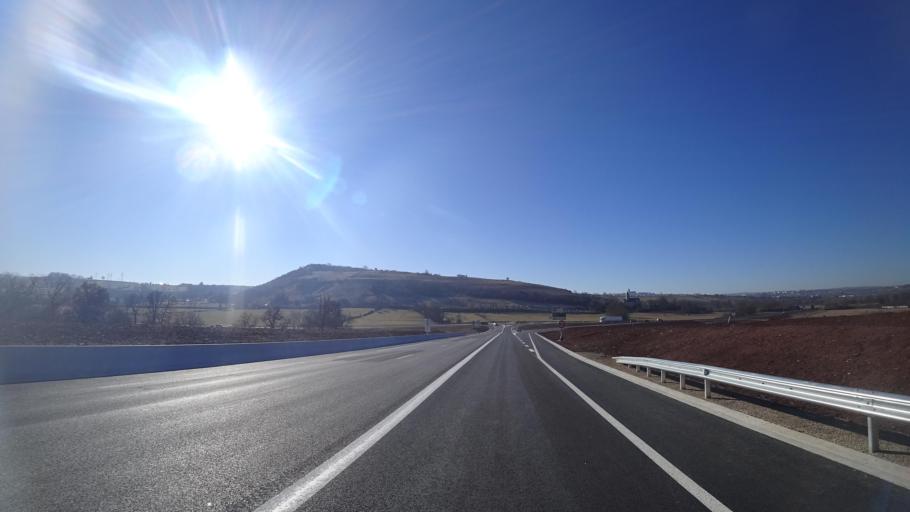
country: FR
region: Midi-Pyrenees
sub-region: Departement de l'Aveyron
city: Sebazac-Concoures
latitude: 44.3769
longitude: 2.6141
